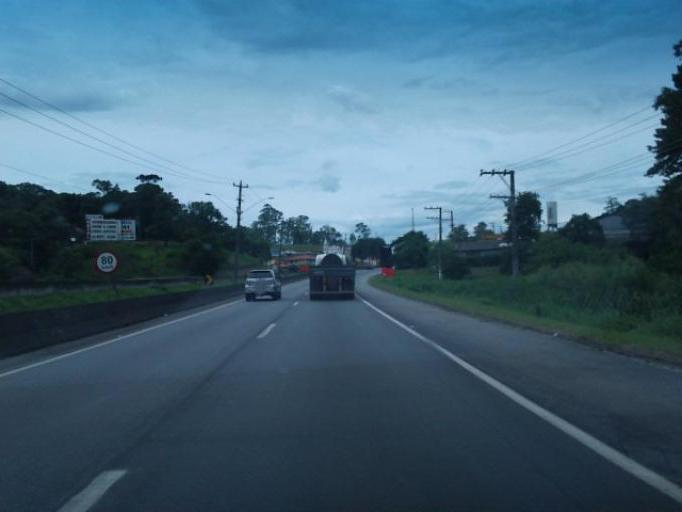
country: BR
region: Sao Paulo
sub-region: Itapecerica Da Serra
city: Itapecerica da Serra
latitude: -23.7387
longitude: -46.8971
